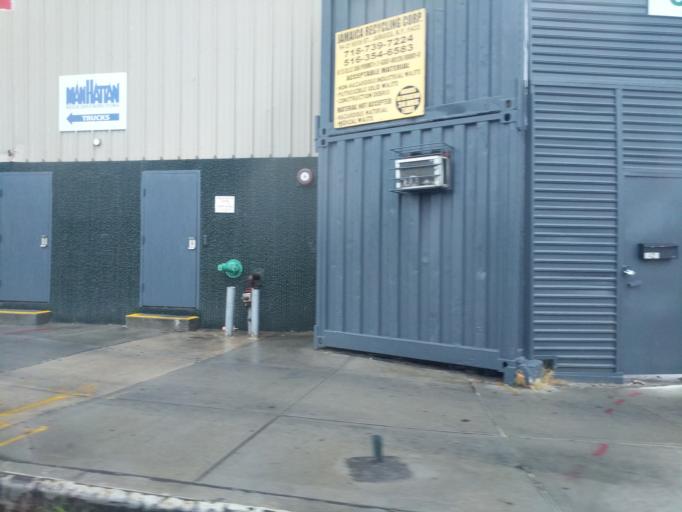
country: US
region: New York
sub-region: Queens County
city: Jamaica
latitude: 40.7024
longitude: -73.7924
